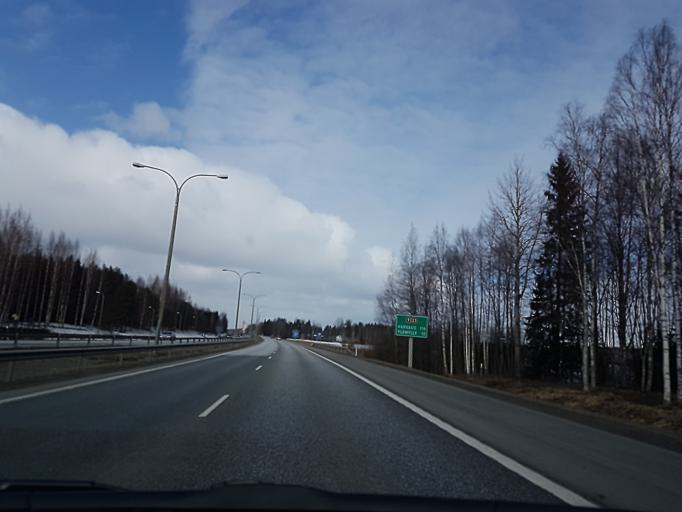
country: FI
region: North Karelia
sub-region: Joensuu
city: Joensuu
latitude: 62.6204
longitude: 29.7245
